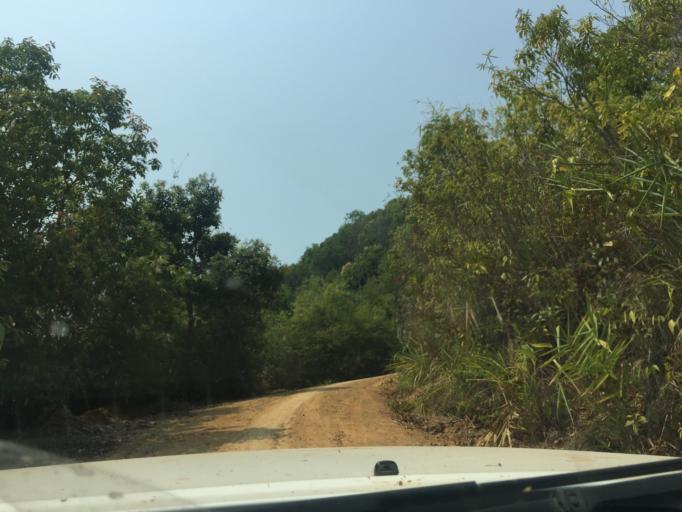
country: LA
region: Loungnamtha
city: Muang Nale
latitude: 20.6300
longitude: 101.6405
